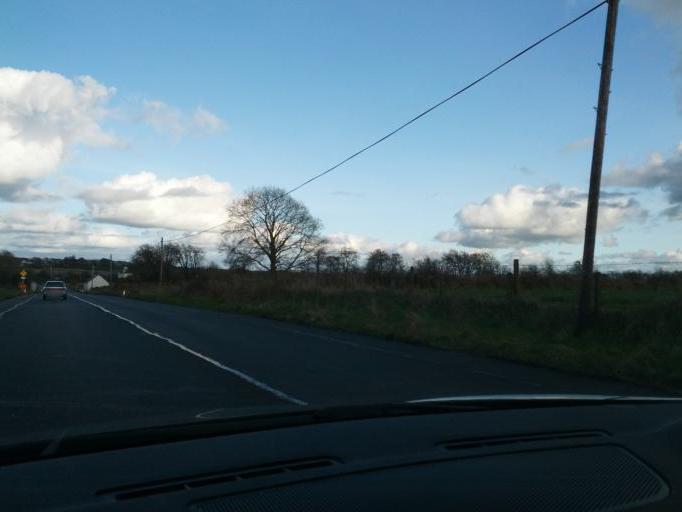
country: IE
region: Connaught
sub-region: Roscommon
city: Castlerea
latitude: 53.6898
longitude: -8.4172
